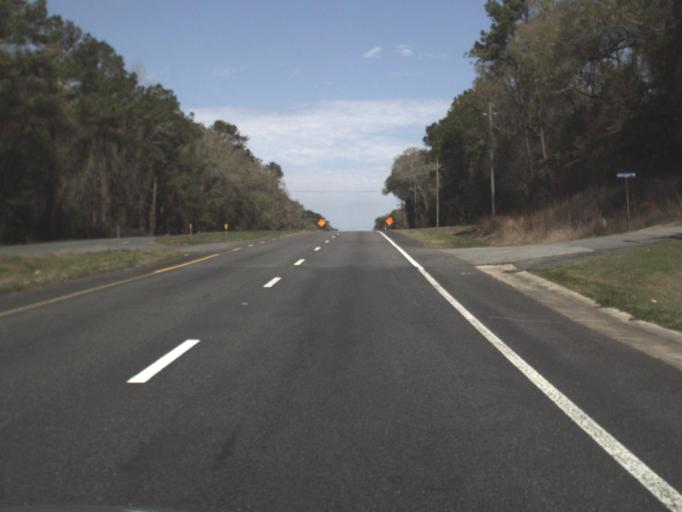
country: US
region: Florida
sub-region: Gadsden County
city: Havana
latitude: 30.5625
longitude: -84.3896
